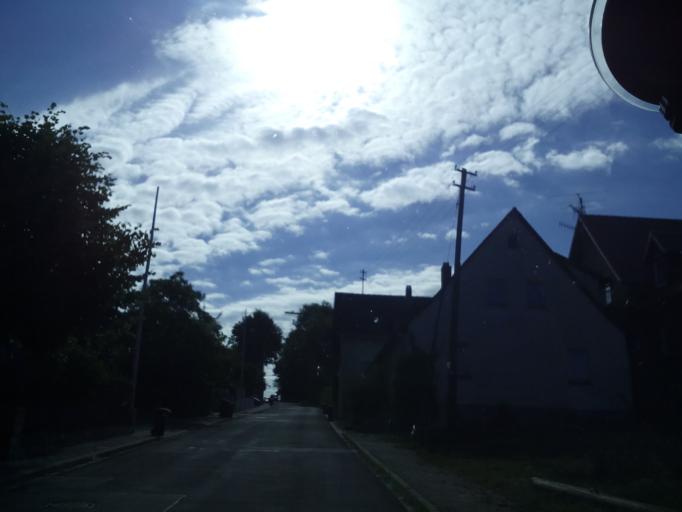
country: DE
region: Bavaria
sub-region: Upper Franconia
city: Eggolsheim
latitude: 49.8076
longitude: 11.0785
